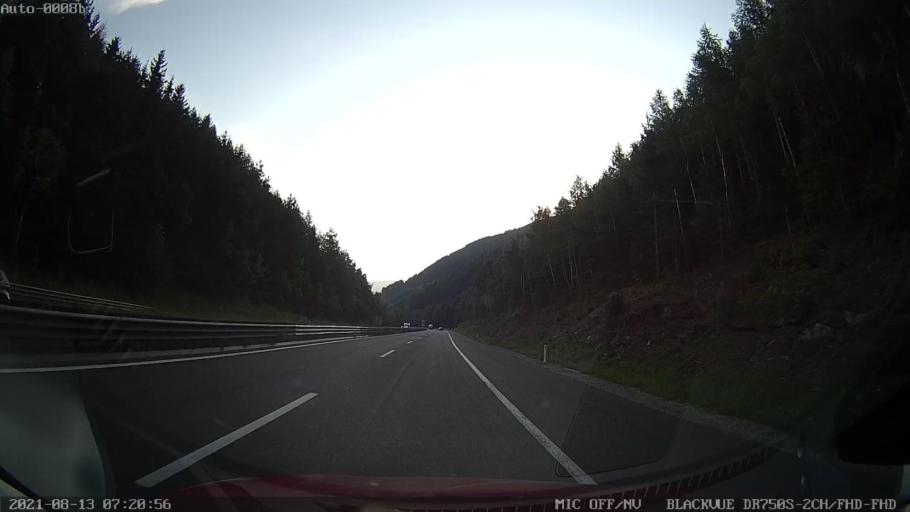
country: AT
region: Carinthia
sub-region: Politischer Bezirk Spittal an der Drau
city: Gmuend
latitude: 46.9091
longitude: 13.5502
